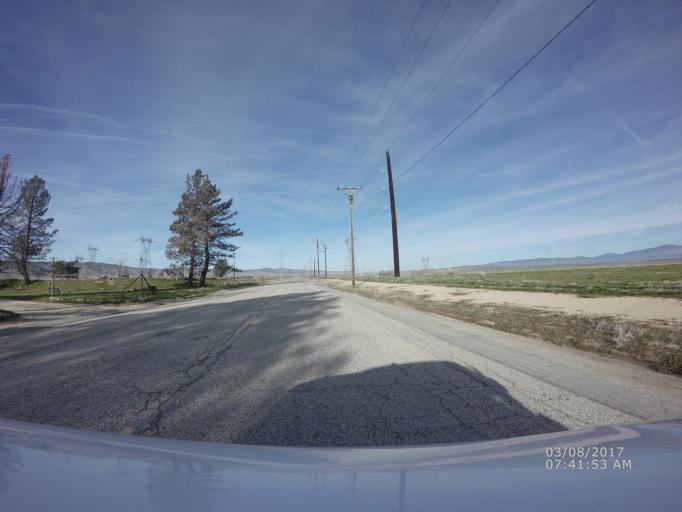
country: US
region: California
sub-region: Los Angeles County
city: Leona Valley
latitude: 34.7038
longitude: -118.3103
